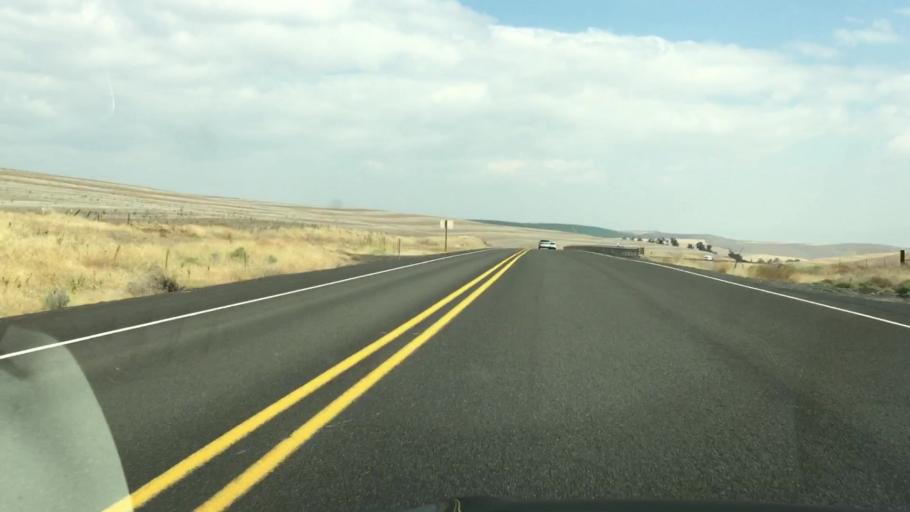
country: US
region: Oregon
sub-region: Wasco County
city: The Dalles
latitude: 45.4669
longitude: -121.1221
